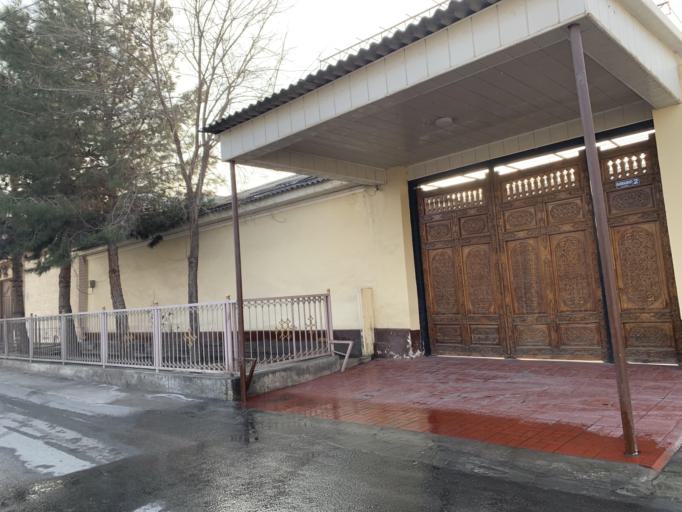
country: UZ
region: Fergana
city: Qo`qon
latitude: 40.5414
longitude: 70.9315
